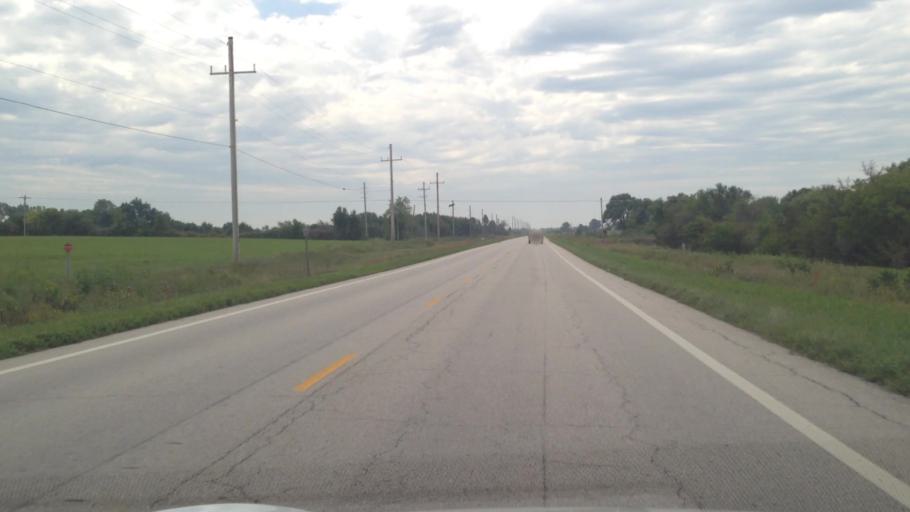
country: US
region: Kansas
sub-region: Allen County
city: Iola
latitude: 37.9526
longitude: -95.1700
